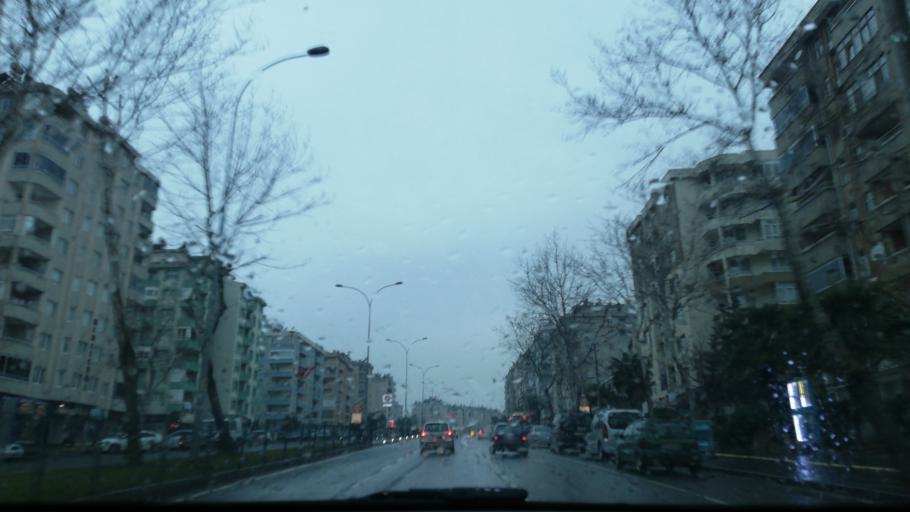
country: TR
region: Kahramanmaras
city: Kahramanmaras
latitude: 37.5842
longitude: 36.9095
